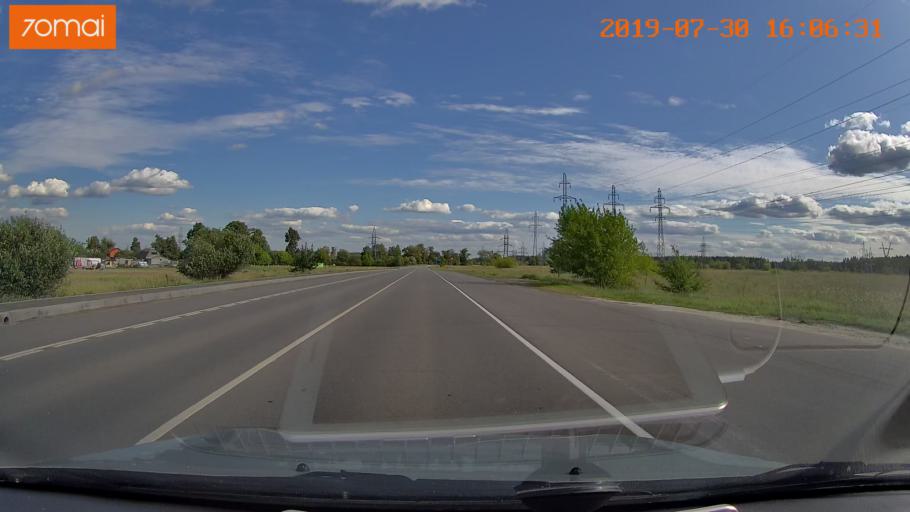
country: RU
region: Moskovskaya
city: Peski
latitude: 55.2551
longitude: 38.7171
